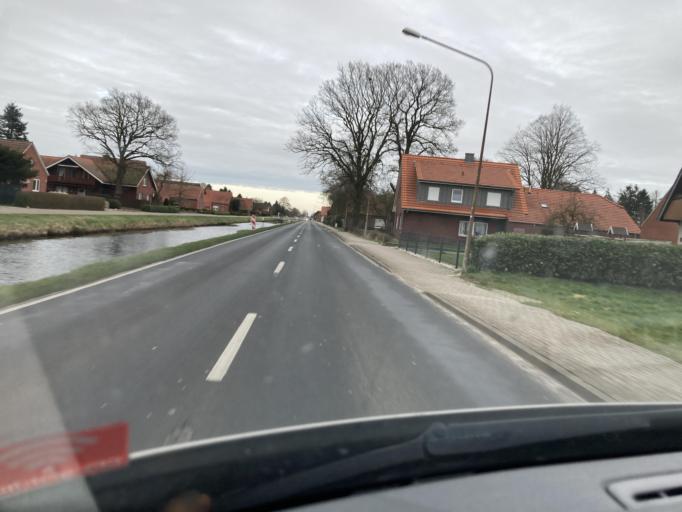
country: DE
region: Lower Saxony
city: Ostrhauderfehn
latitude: 53.1311
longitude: 7.5259
